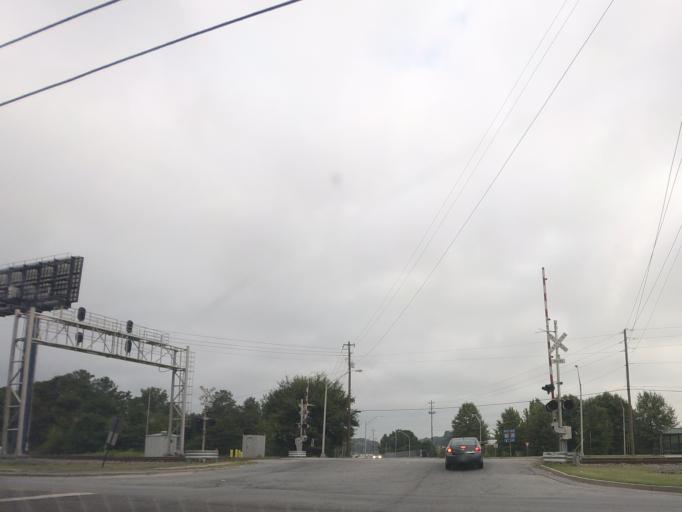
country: US
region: Georgia
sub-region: Fulton County
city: Hapeville
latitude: 33.6637
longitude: -84.4183
